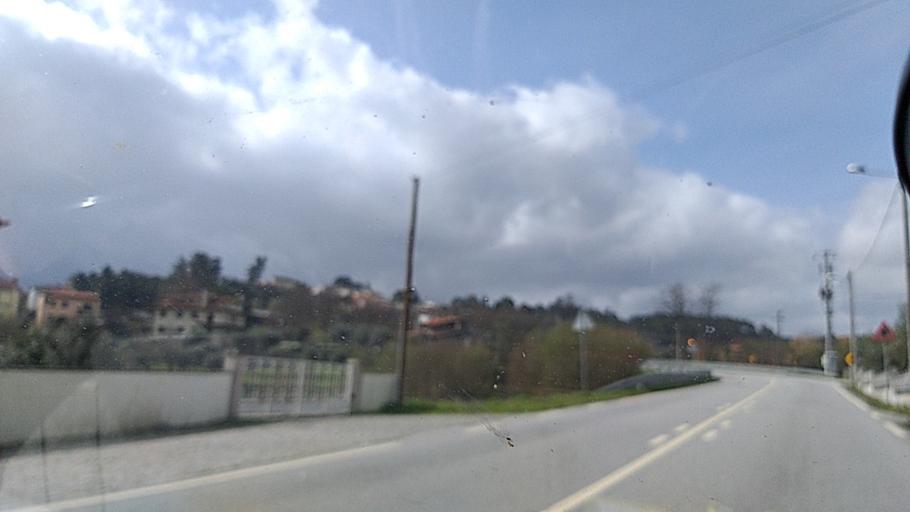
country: PT
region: Viseu
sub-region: Mangualde
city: Mangualde
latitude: 40.6273
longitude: -7.7526
